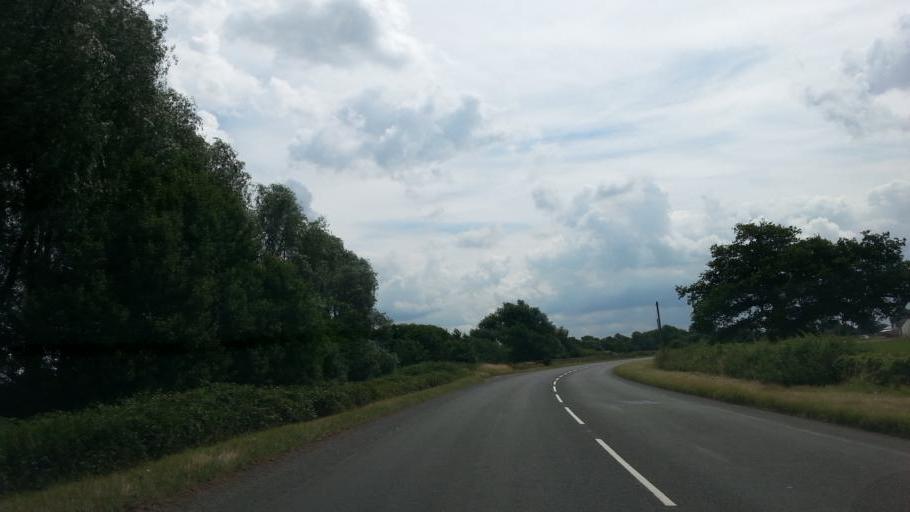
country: GB
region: England
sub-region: Staffordshire
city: Alrewas
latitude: 52.7448
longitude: -1.7915
